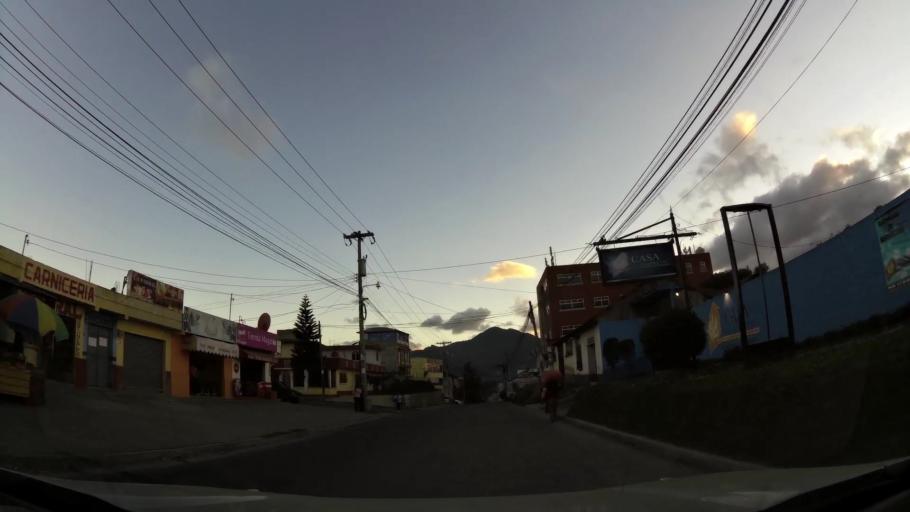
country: GT
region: Quetzaltenango
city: Quetzaltenango
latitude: 14.8545
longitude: -91.5122
